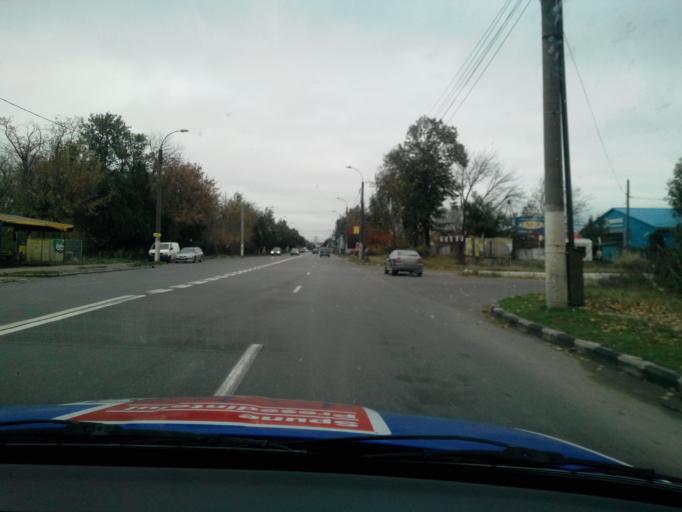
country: RO
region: Giurgiu
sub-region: Comuna Fratesti
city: Remus
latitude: 43.9222
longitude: 25.9736
